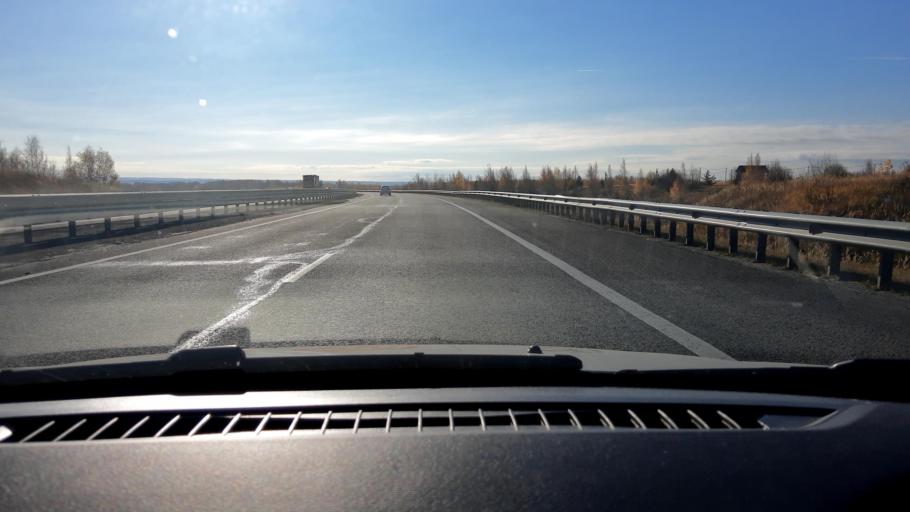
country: RU
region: Nizjnij Novgorod
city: Burevestnik
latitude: 56.1510
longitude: 43.7494
